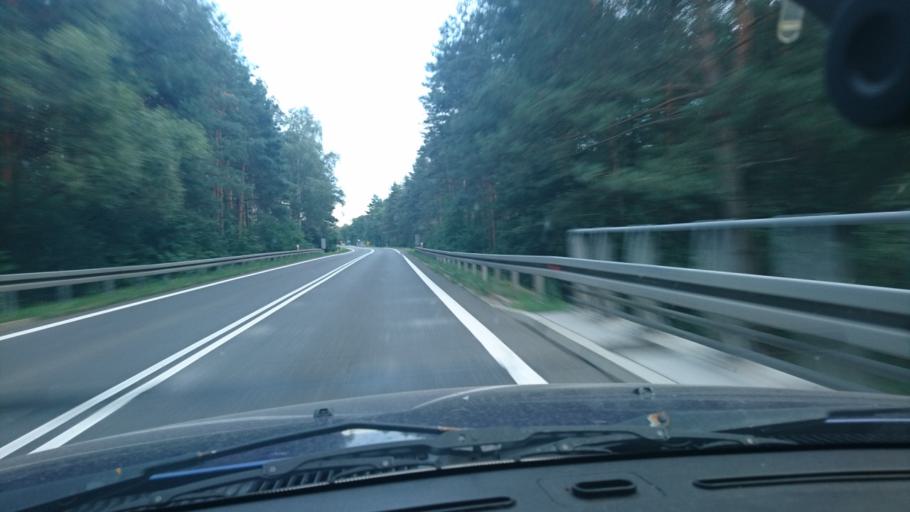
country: PL
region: Silesian Voivodeship
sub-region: Powiat tarnogorski
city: Tworog
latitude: 50.5909
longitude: 18.7010
